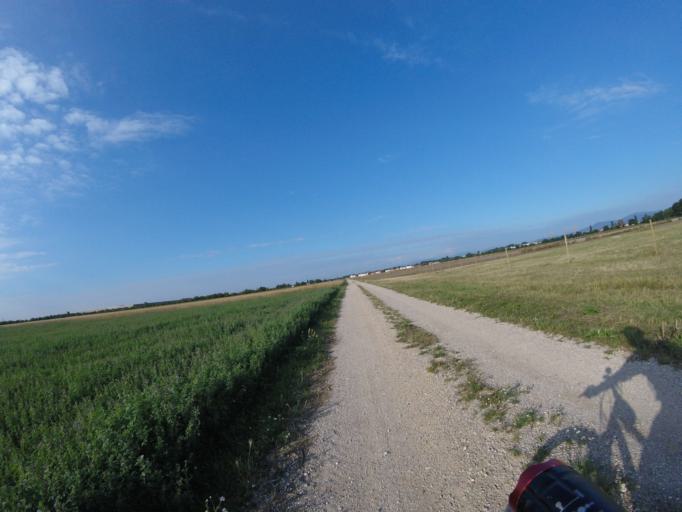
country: AT
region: Lower Austria
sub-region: Politischer Bezirk Baden
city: Trumau
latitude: 48.0024
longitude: 16.3611
